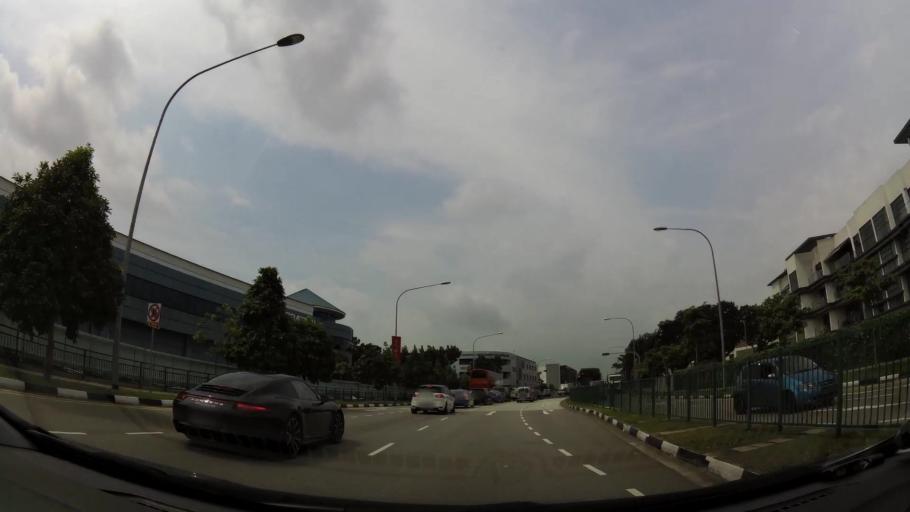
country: SG
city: Singapore
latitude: 1.3539
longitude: 103.9682
